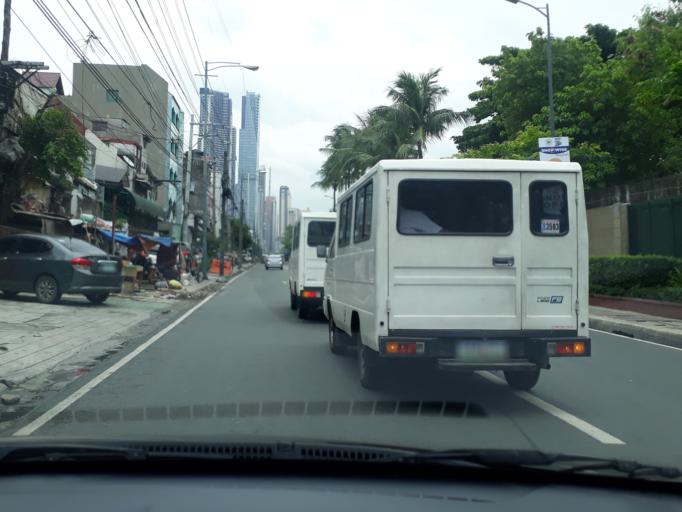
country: PH
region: Metro Manila
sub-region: Makati City
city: Makati City
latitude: 14.5682
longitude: 121.0193
